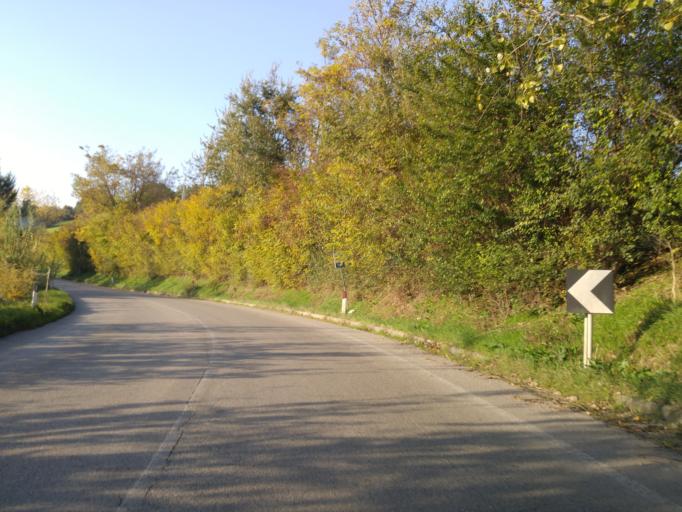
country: IT
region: The Marches
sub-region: Provincia di Pesaro e Urbino
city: Tavernelle
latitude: 43.7282
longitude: 12.8783
